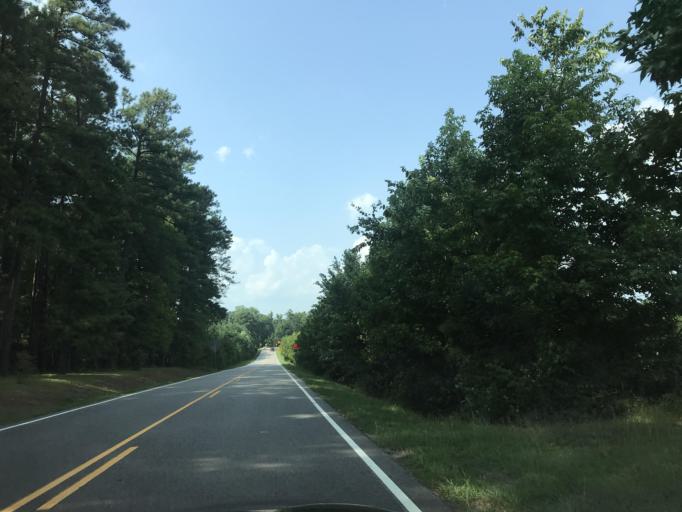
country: US
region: North Carolina
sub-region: Wake County
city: Morrisville
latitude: 35.8270
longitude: -78.8635
